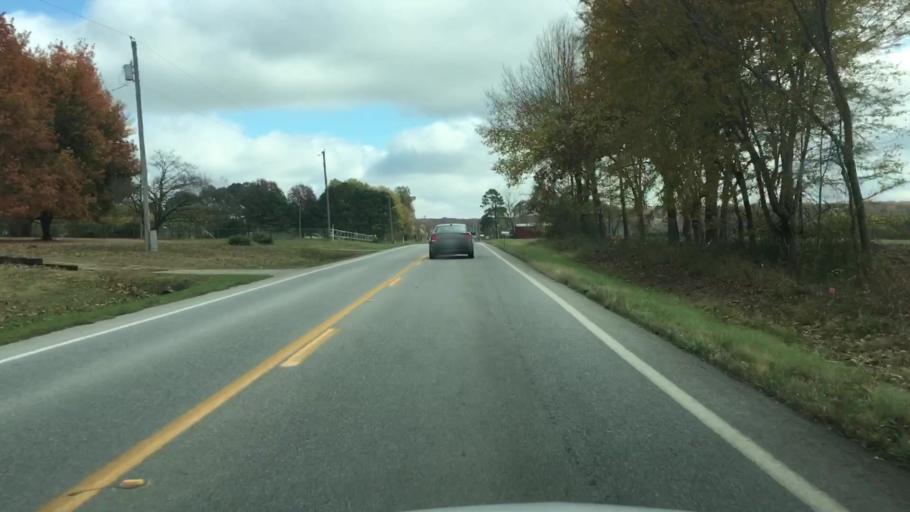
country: US
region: Arkansas
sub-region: Benton County
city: Gentry
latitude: 36.2559
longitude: -94.4460
